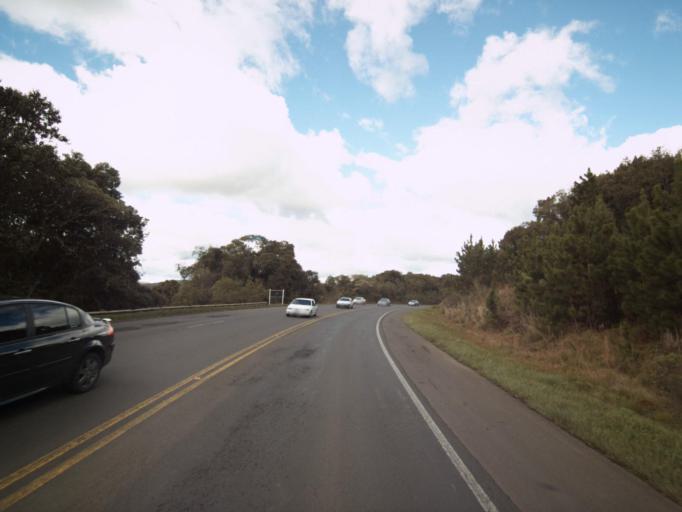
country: BR
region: Santa Catarina
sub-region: Joacaba
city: Joacaba
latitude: -27.0405
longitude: -51.7079
